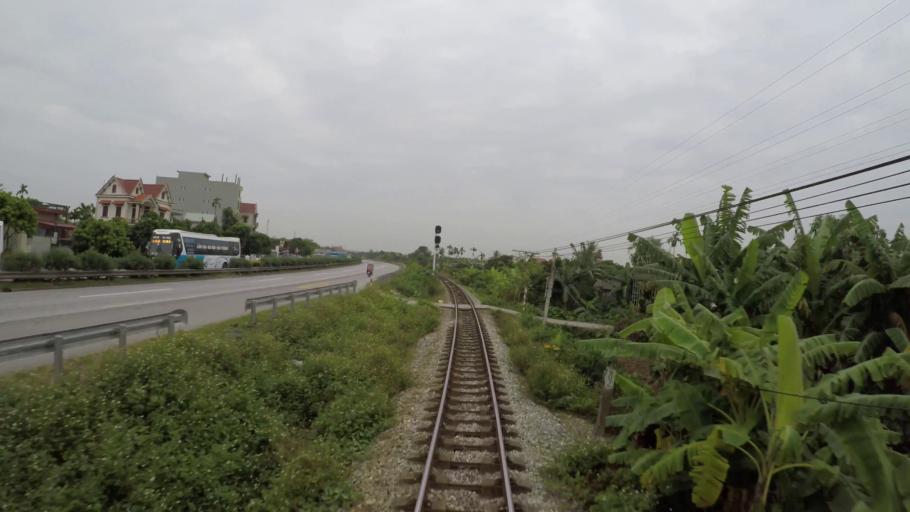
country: VN
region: Hai Duong
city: Phu Thai
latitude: 20.9753
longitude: 106.4342
